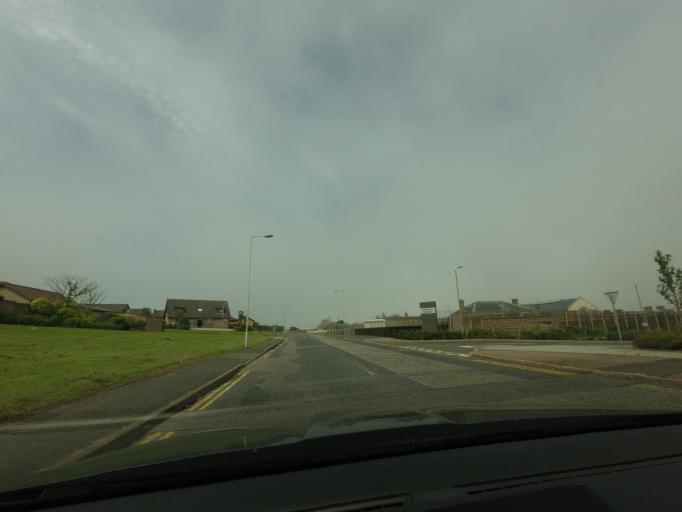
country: GB
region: Scotland
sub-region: Aberdeenshire
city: Peterhead
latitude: 57.4904
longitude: -1.7927
